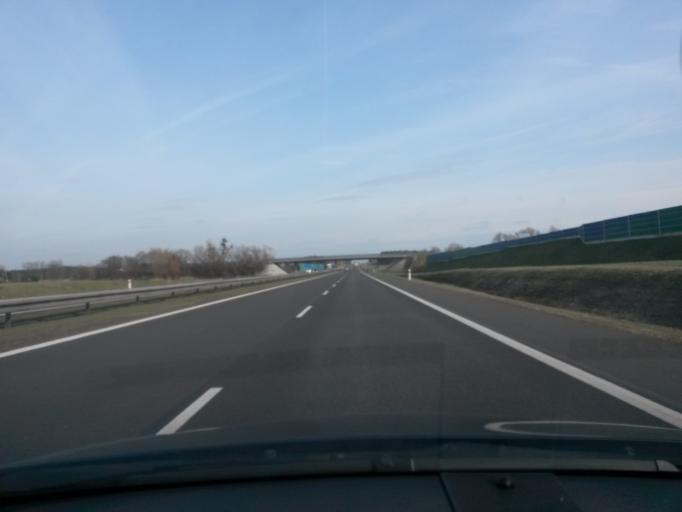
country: PL
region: Greater Poland Voivodeship
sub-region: Powiat slupecki
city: Slupca
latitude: 52.2496
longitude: 17.8407
